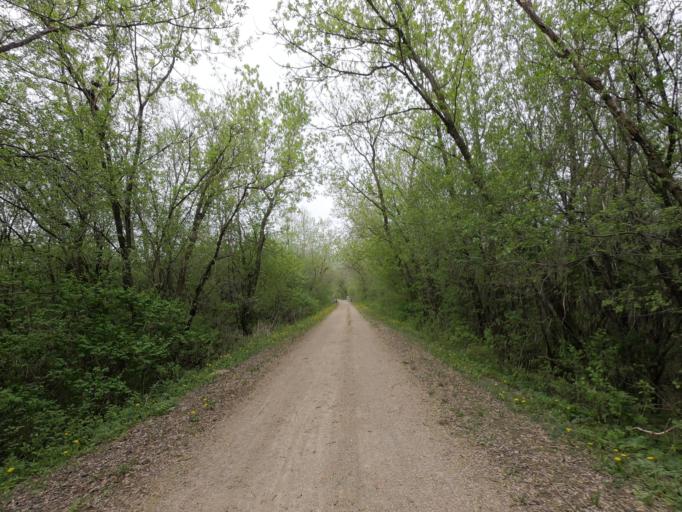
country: US
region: Wisconsin
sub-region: Jefferson County
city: Johnson Creek
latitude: 43.0366
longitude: -88.7620
